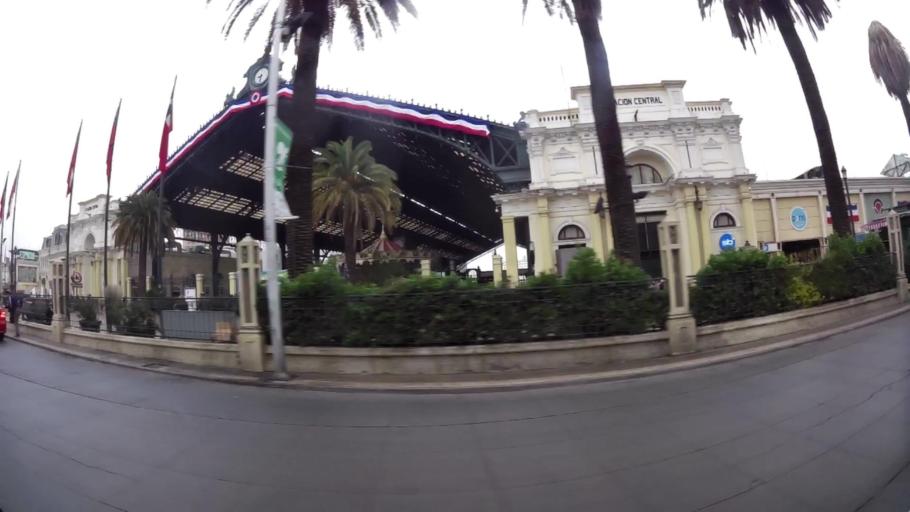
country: CL
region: Santiago Metropolitan
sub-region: Provincia de Santiago
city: Santiago
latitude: -33.4510
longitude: -70.6792
